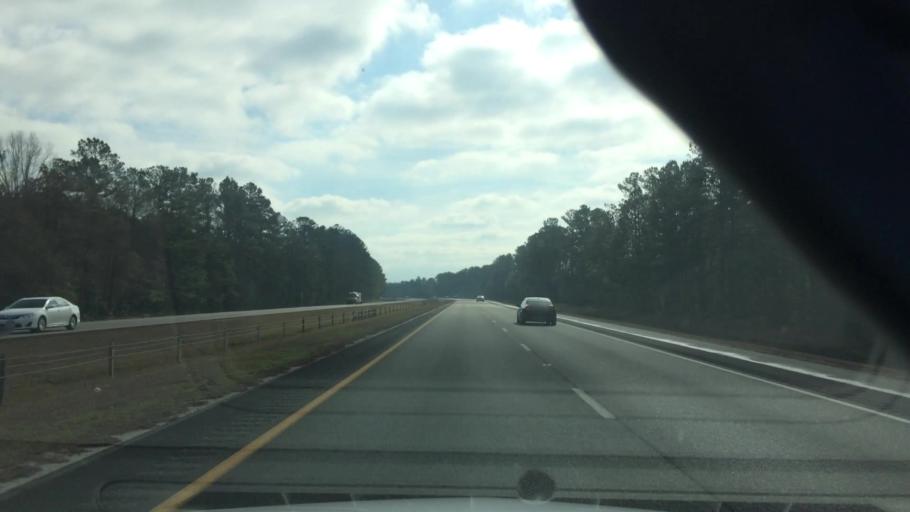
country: US
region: North Carolina
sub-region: Pender County
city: Burgaw
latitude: 34.5406
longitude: -77.8935
